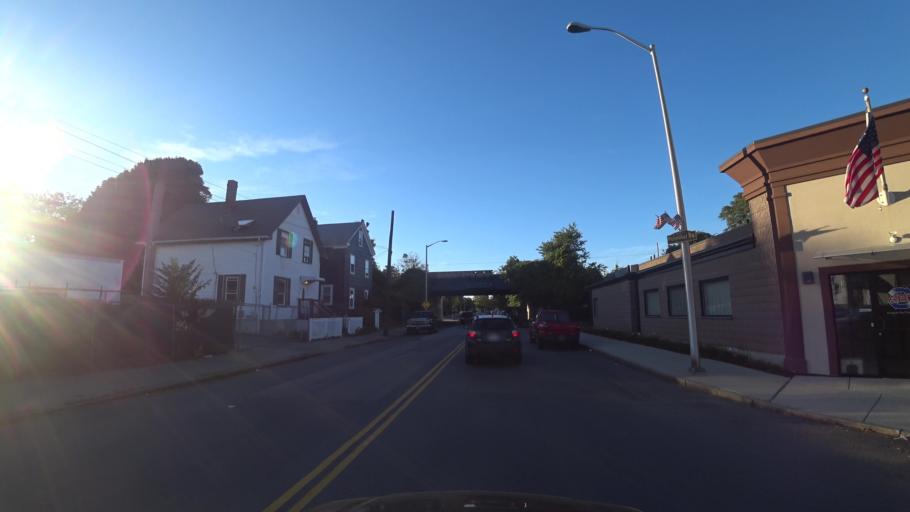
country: US
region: Massachusetts
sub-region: Essex County
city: Lynn
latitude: 42.4590
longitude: -70.9524
